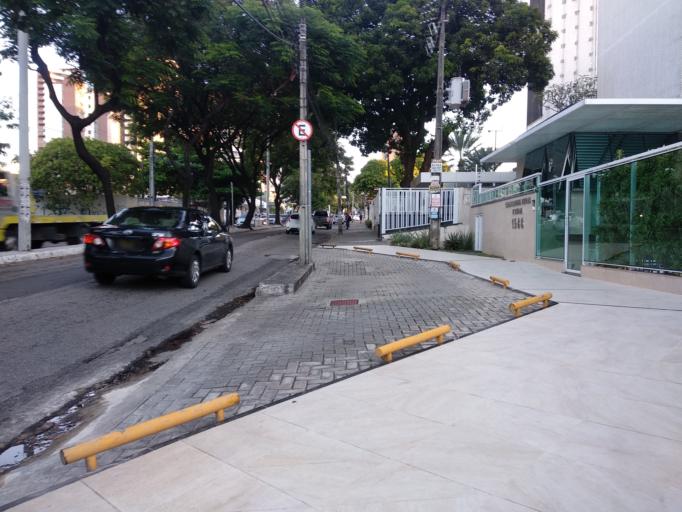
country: BR
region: Ceara
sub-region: Fortaleza
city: Fortaleza
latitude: -3.7404
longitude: -38.5085
